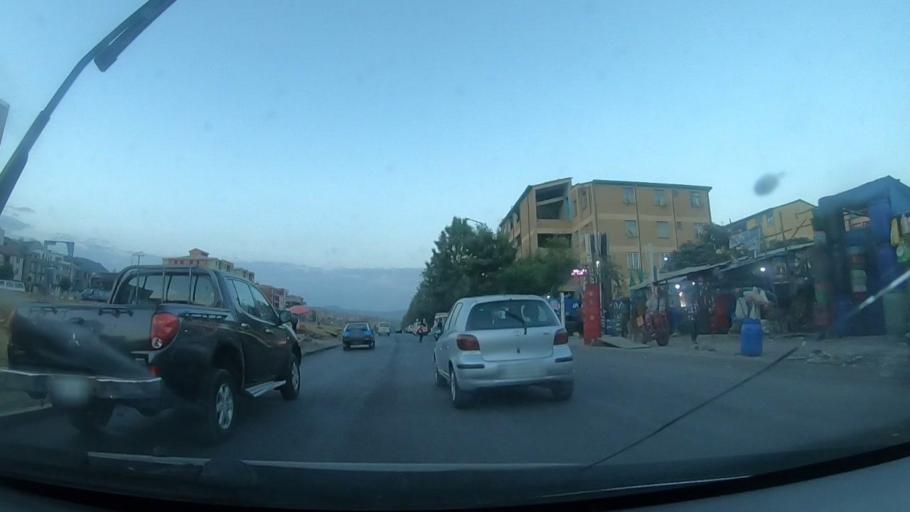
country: ET
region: Adis Abeba
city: Addis Ababa
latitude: 9.0353
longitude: 38.8779
